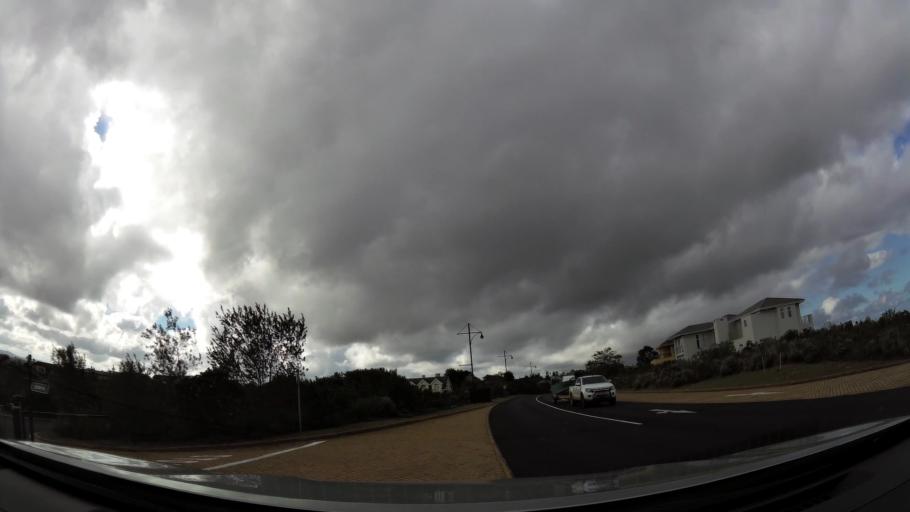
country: ZA
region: Western Cape
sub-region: Eden District Municipality
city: Knysna
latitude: -34.0675
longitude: 23.0944
